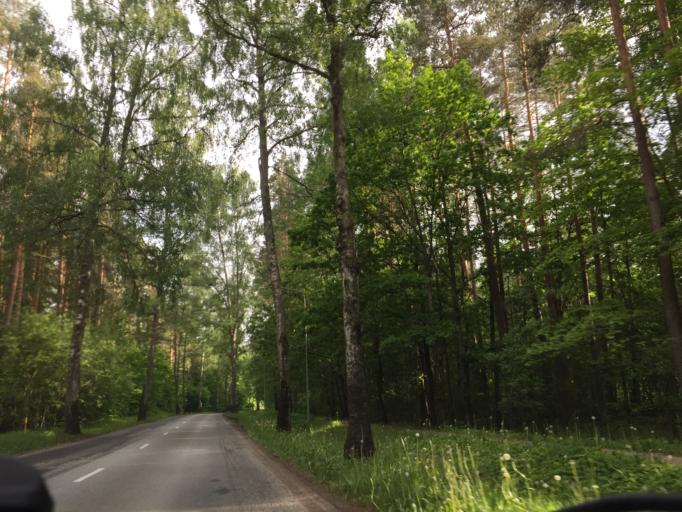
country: LV
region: Valmieras Rajons
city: Valmiera
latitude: 57.5253
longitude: 25.4211
